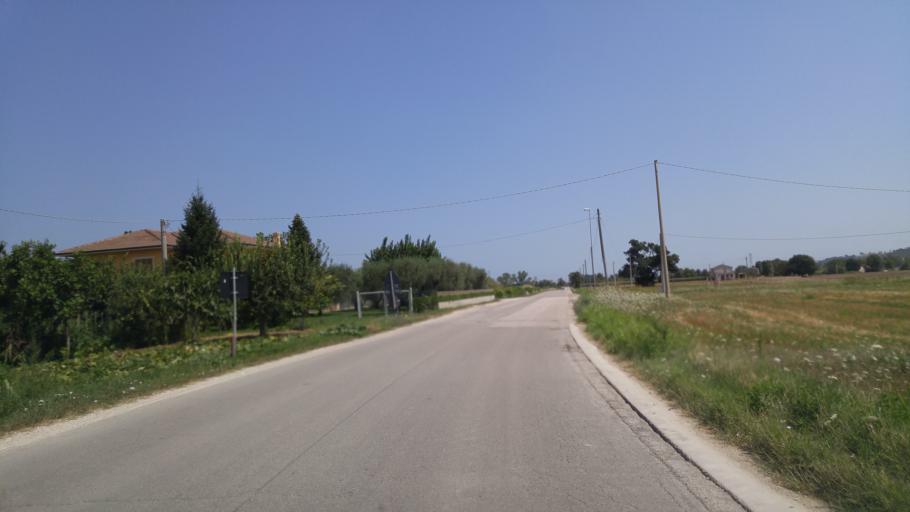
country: IT
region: The Marches
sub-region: Provincia di Pesaro e Urbino
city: Lucrezia
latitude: 43.7654
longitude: 12.9676
